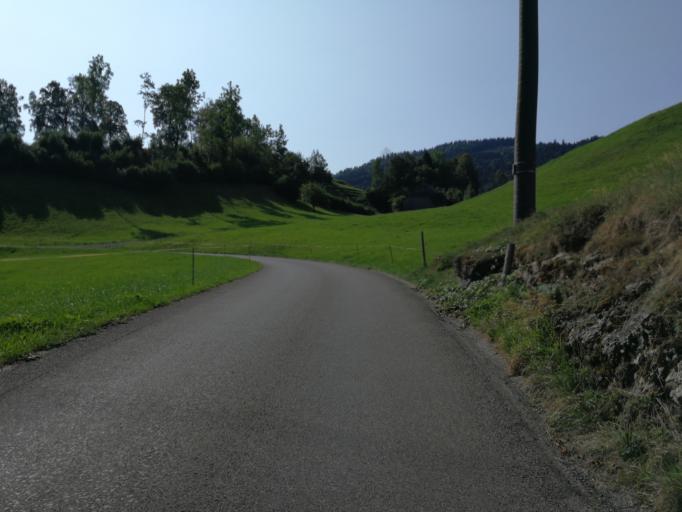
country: CH
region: Saint Gallen
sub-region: Wahlkreis Toggenburg
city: Ebnat-Kappel
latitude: 47.2524
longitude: 9.1454
